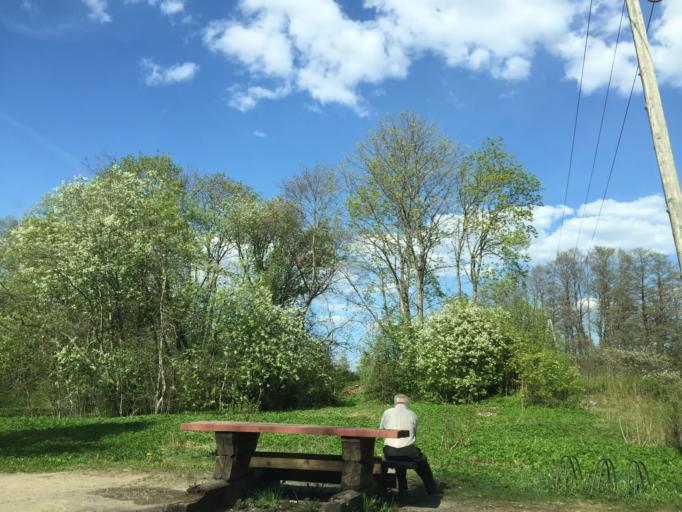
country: LV
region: Limbazu Rajons
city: Limbazi
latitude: 57.5068
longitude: 24.6965
